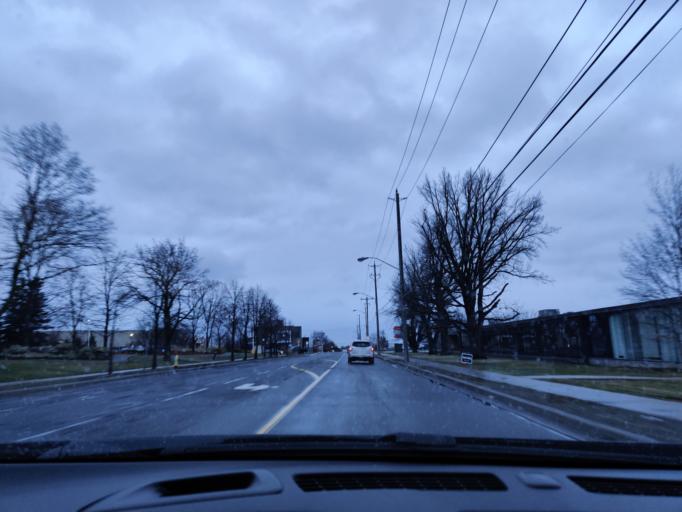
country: CA
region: Ontario
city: Toronto
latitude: 43.7016
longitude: -79.4643
